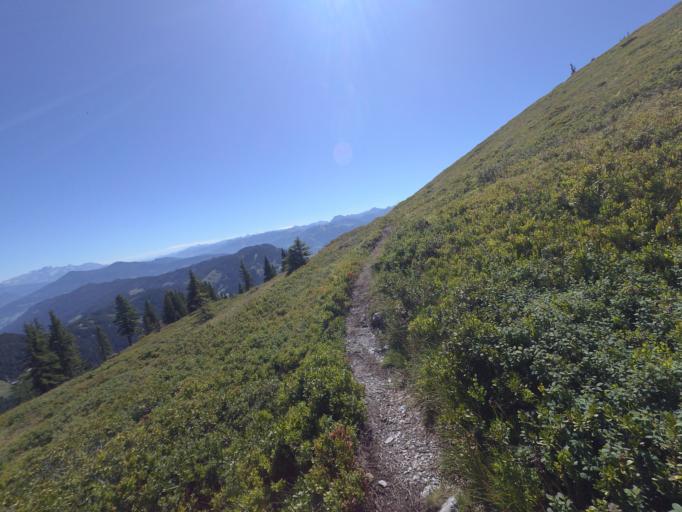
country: AT
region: Salzburg
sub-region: Politischer Bezirk Sankt Johann im Pongau
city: Goldegg
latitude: 47.3585
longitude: 13.0739
